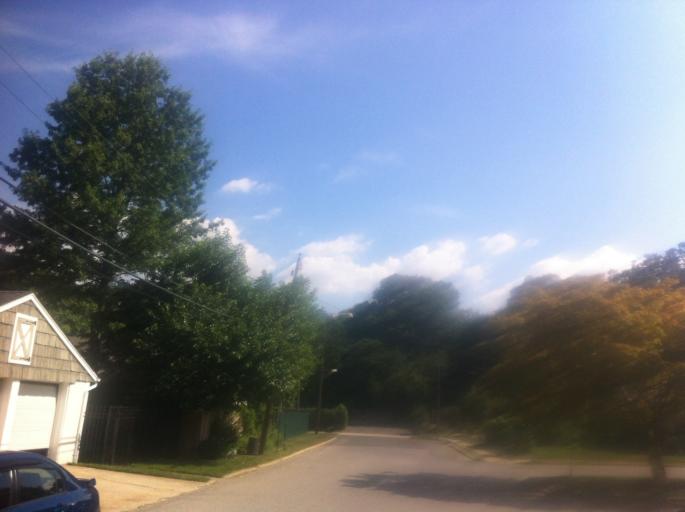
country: US
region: New York
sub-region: Nassau County
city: Glen Cove
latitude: 40.8563
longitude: -73.6122
